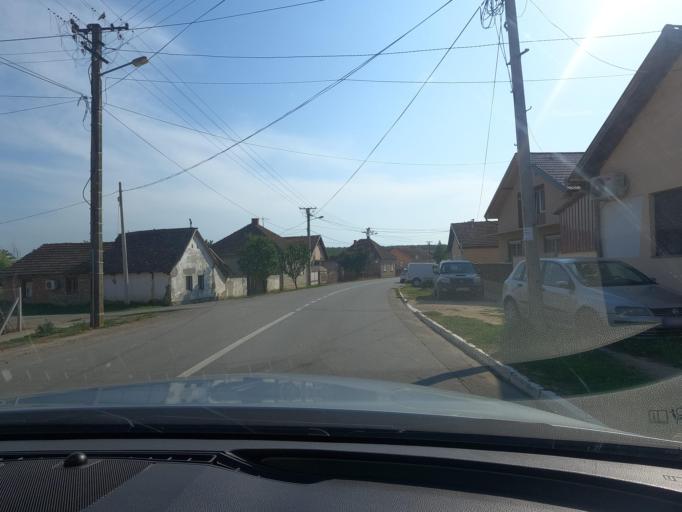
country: RS
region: Autonomna Pokrajina Vojvodina
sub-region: Juznobacki Okrug
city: Kovilj
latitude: 45.2183
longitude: 20.0327
